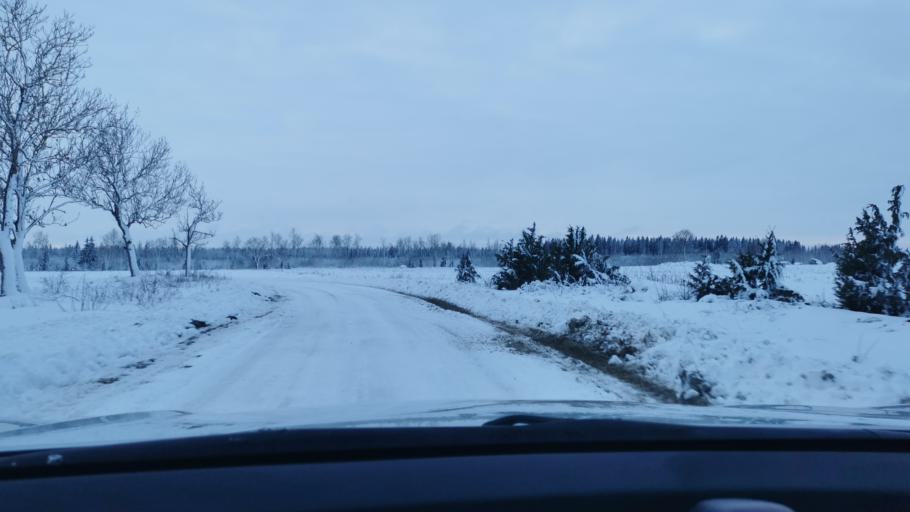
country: EE
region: Laeaene-Virumaa
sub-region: Viru-Nigula vald
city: Kunda
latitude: 59.4906
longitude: 26.4061
